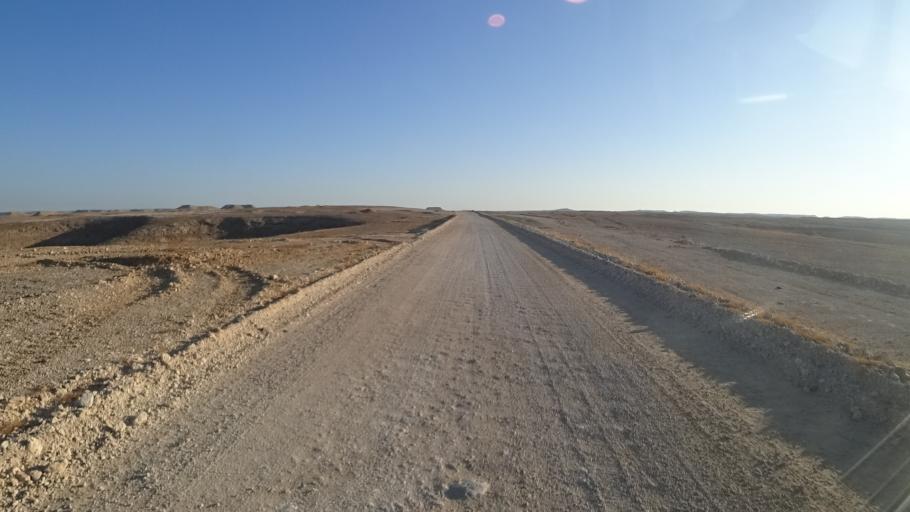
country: YE
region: Al Mahrah
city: Hawf
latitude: 17.1675
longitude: 53.3521
